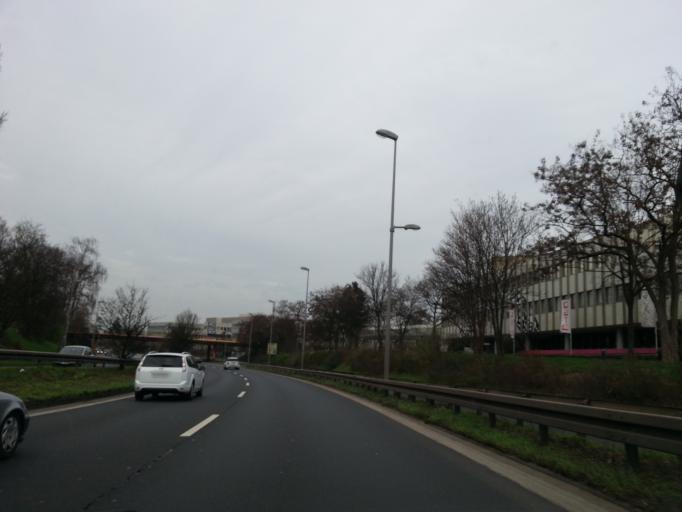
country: DE
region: North Rhine-Westphalia
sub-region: Regierungsbezirk Dusseldorf
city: Dusseldorf
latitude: 51.2607
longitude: 6.7618
